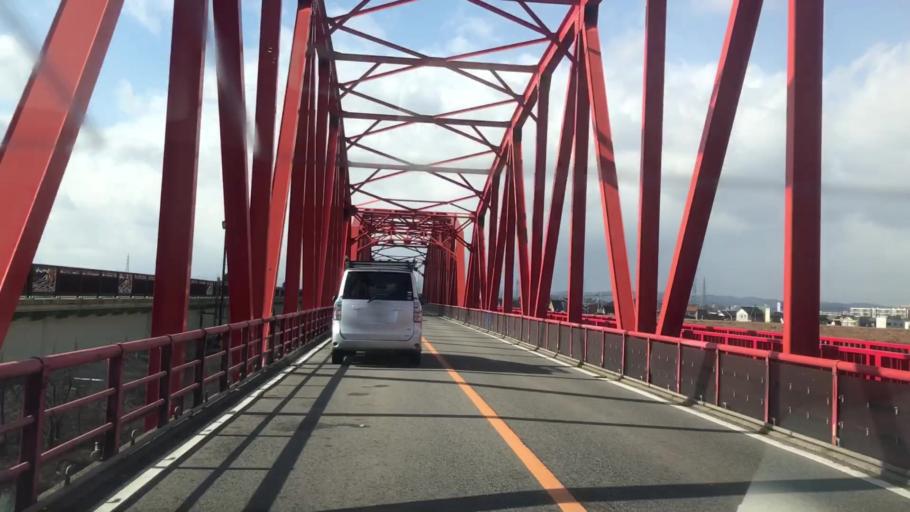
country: JP
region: Toyama
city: Takaoka
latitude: 36.7350
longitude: 137.0441
